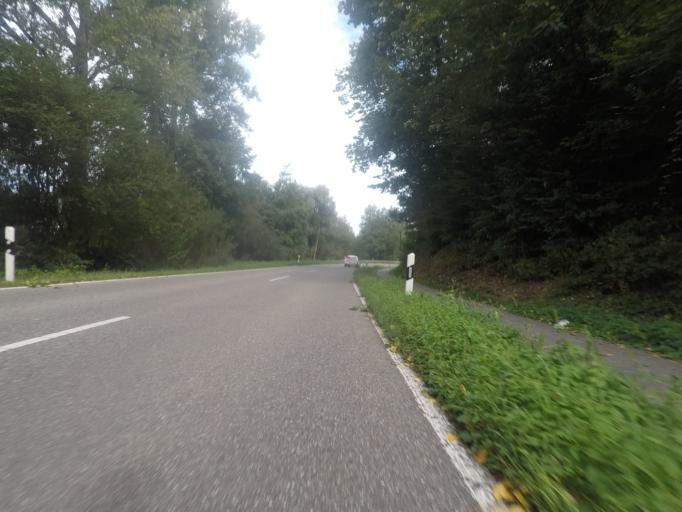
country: DE
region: Baden-Wuerttemberg
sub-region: Karlsruhe Region
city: Malsch
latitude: 48.8647
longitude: 8.3326
